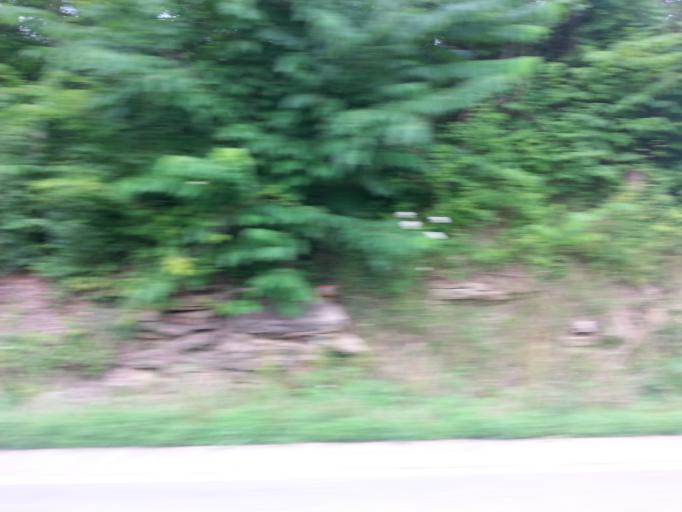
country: US
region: Kentucky
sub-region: Harrison County
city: Cynthiana
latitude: 38.4653
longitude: -84.2404
